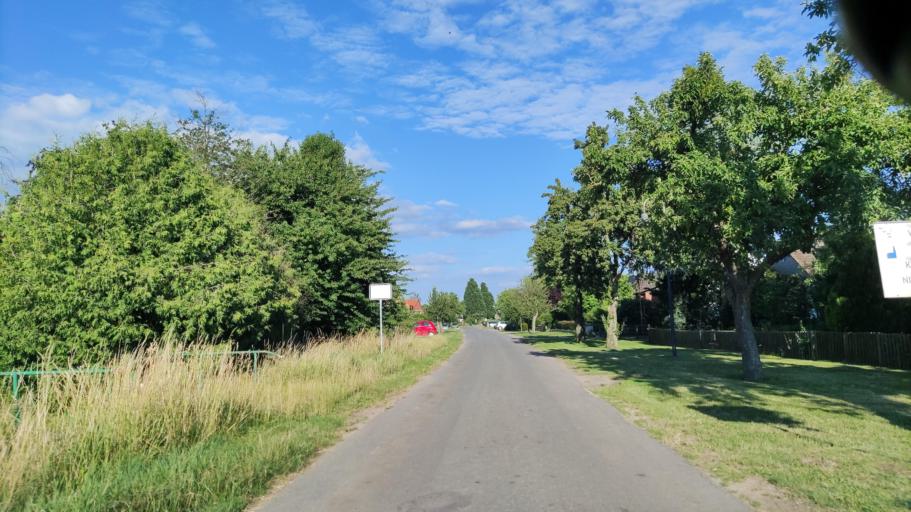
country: DE
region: Brandenburg
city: Lanz
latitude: 53.0395
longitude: 11.5545
